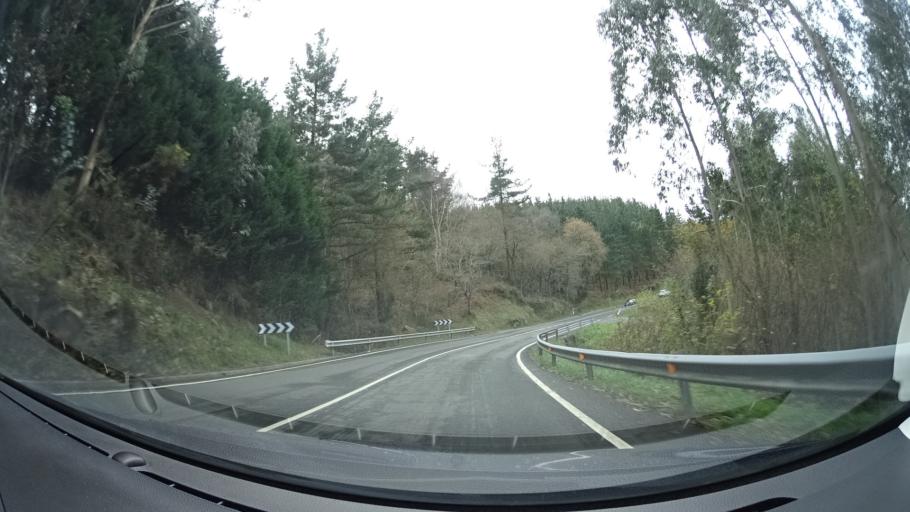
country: ES
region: Basque Country
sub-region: Bizkaia
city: Bermeo
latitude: 43.3957
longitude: -2.7677
